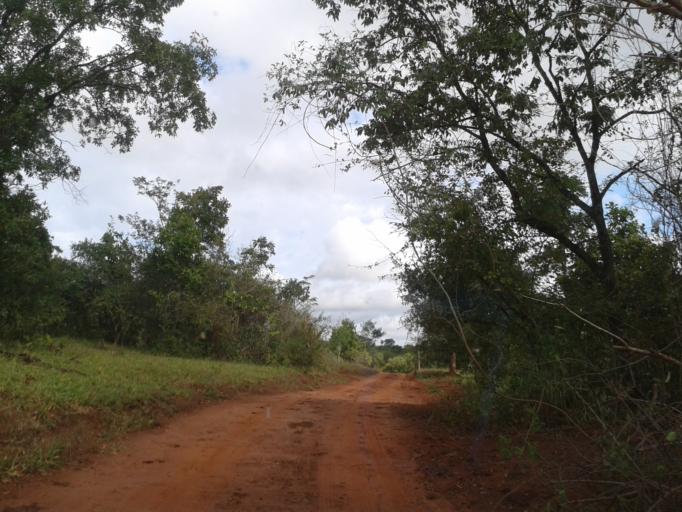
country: BR
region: Minas Gerais
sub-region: Campina Verde
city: Campina Verde
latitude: -19.4923
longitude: -49.6087
